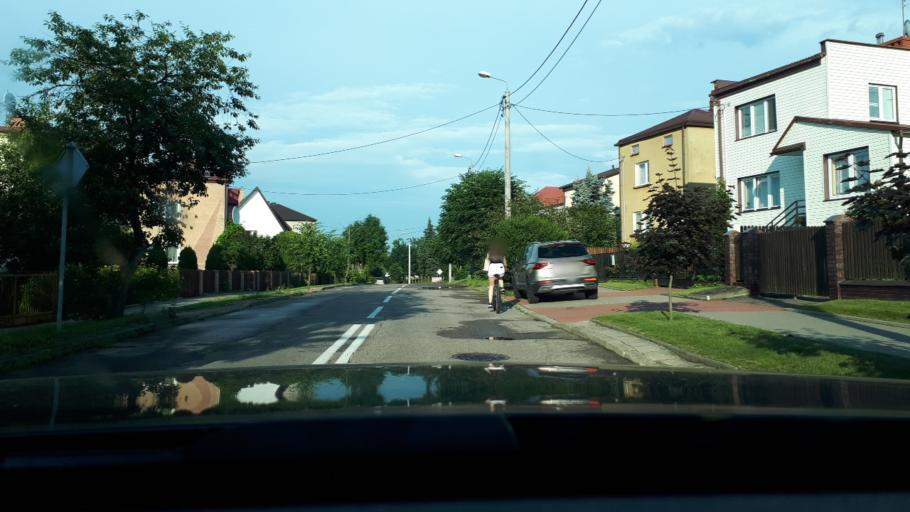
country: PL
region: Podlasie
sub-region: Powiat bialostocki
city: Suprasl
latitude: 53.2060
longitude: 23.3310
